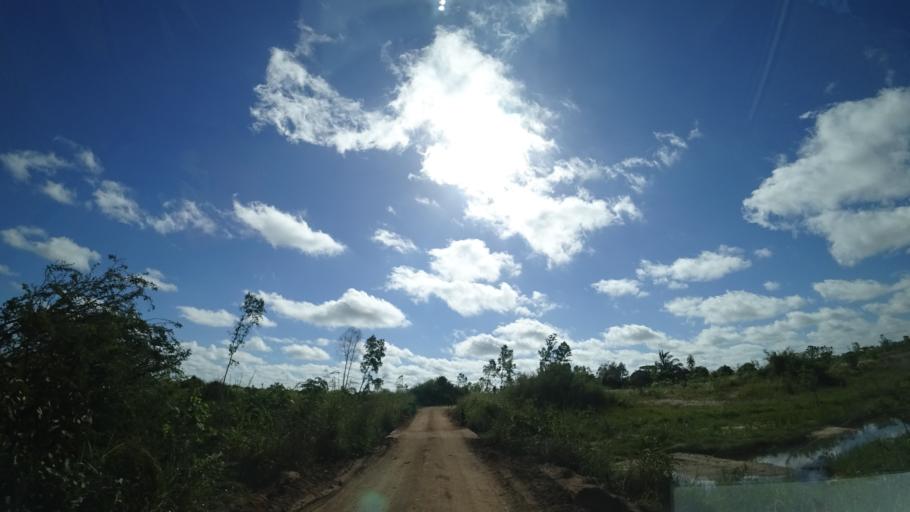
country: MZ
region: Sofala
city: Dondo
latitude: -19.4247
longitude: 34.7080
